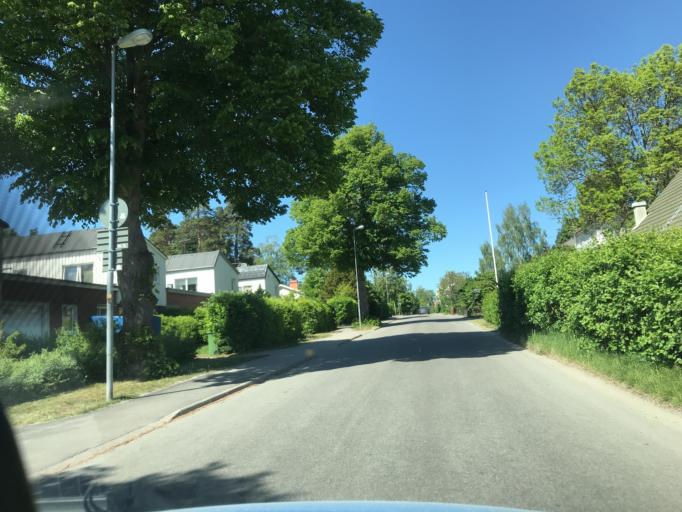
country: SE
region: Stockholm
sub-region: Sollentuna Kommun
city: Sollentuna
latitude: 59.4127
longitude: 17.9731
